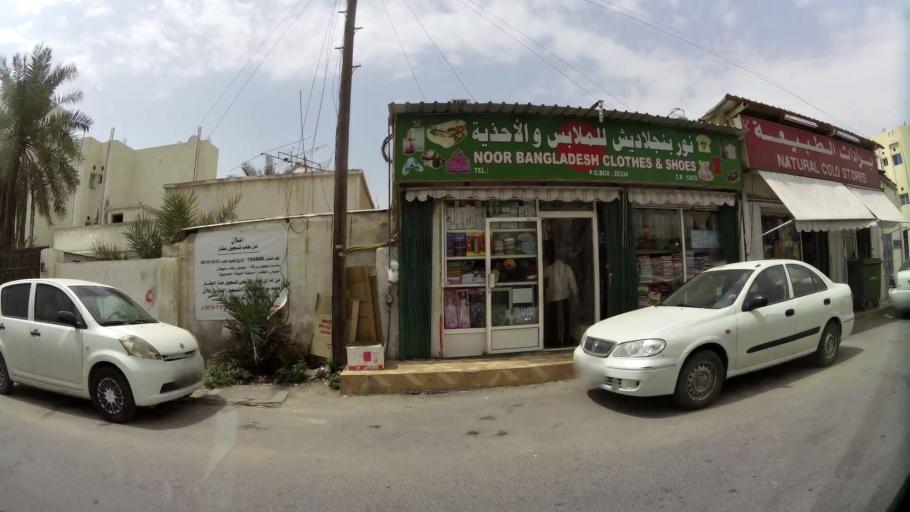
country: QA
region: Baladiyat ar Rayyan
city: Ar Rayyan
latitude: 25.3199
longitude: 51.4736
